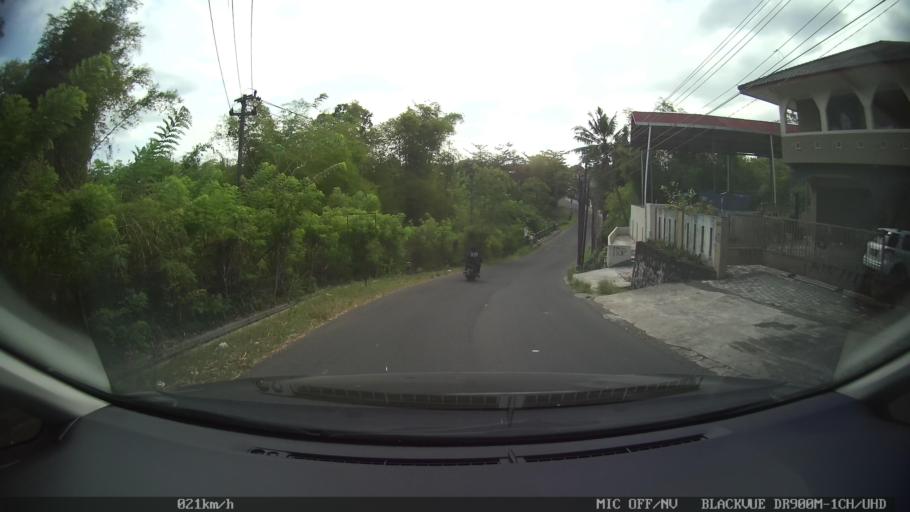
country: ID
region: Daerah Istimewa Yogyakarta
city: Depok
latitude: -7.7361
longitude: 110.4159
